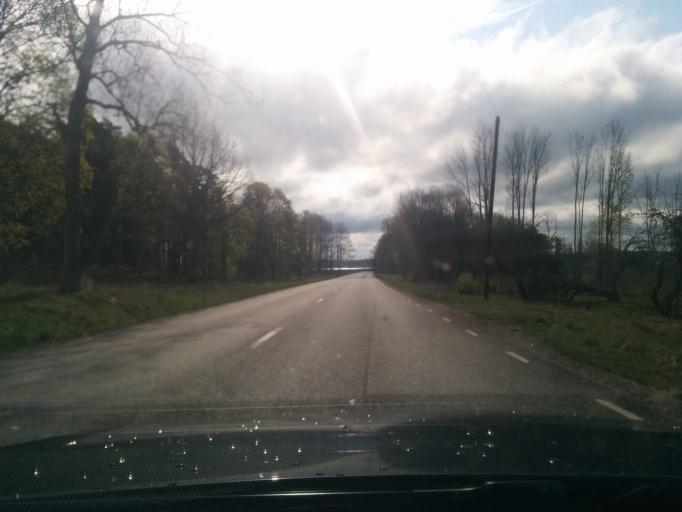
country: SE
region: Uppsala
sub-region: Tierps Kommun
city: Orbyhus
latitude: 60.1766
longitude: 17.6247
